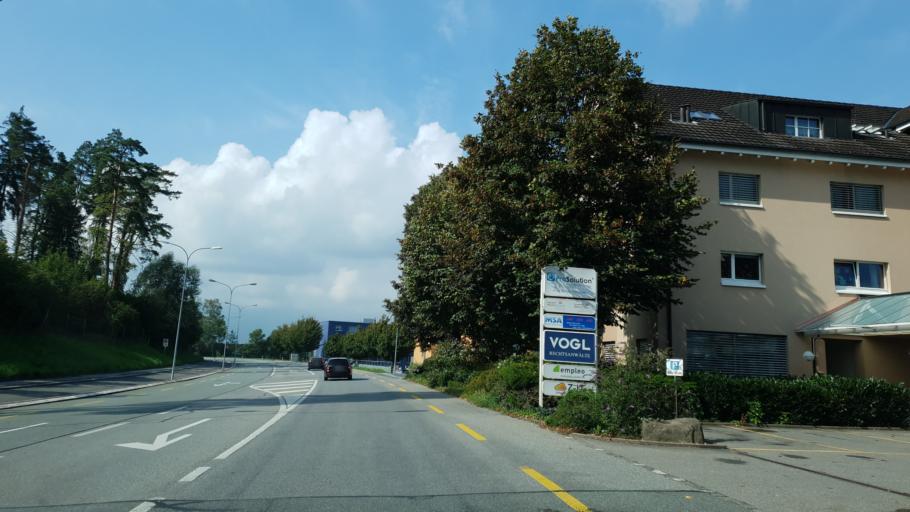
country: LI
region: Mauren
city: Mauren
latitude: 47.2086
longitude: 9.5530
